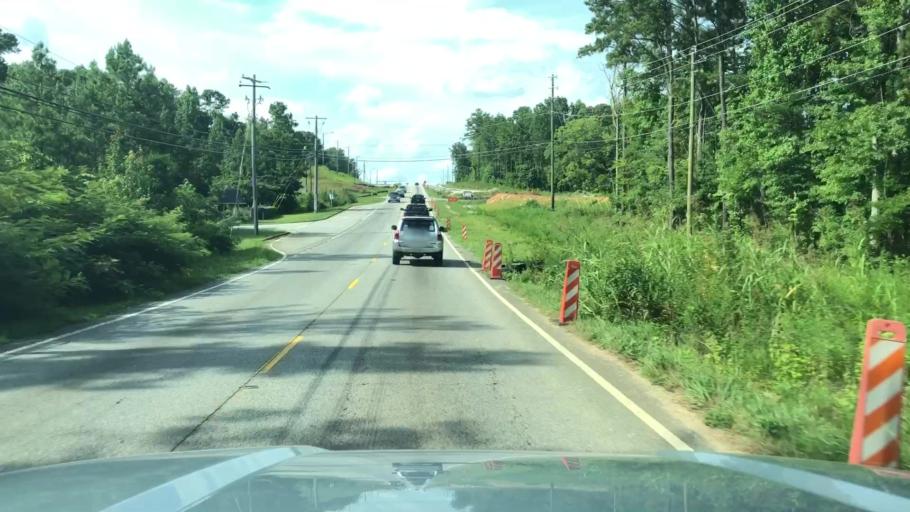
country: US
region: Georgia
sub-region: Douglas County
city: Douglasville
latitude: 33.7635
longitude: -84.7487
